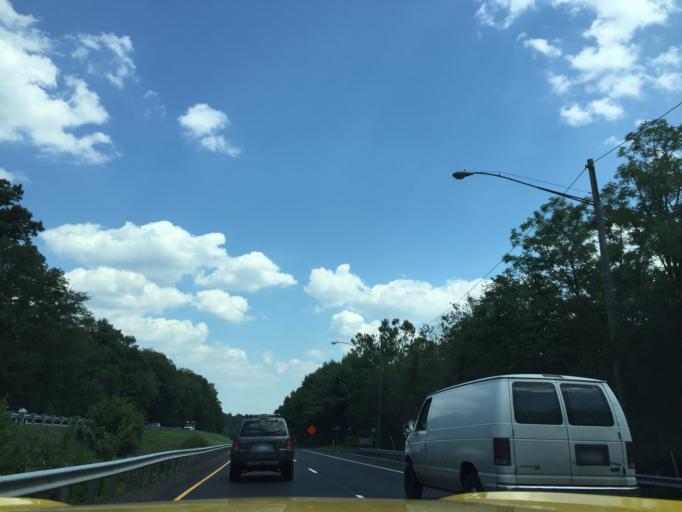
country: US
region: Virginia
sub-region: Fairfax County
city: Great Falls
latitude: 38.9709
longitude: -77.2987
